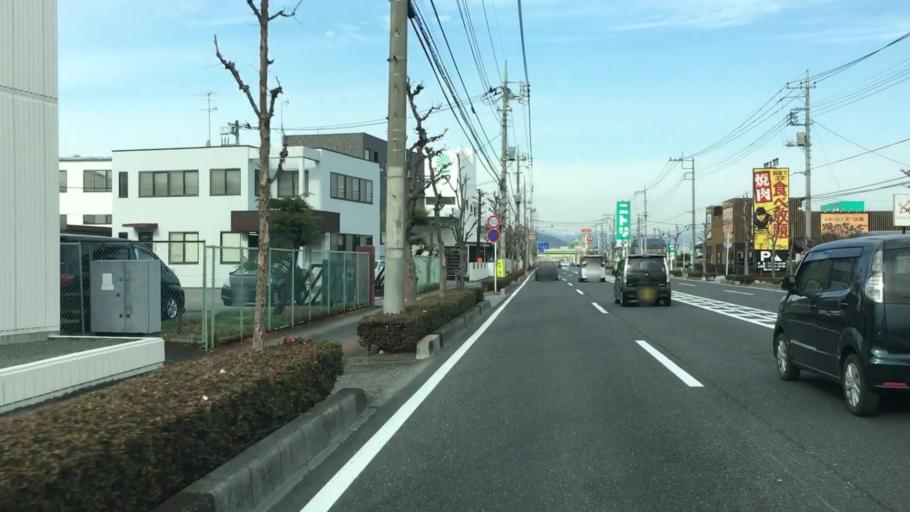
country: JP
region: Gunma
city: Ota
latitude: 36.2645
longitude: 139.3769
